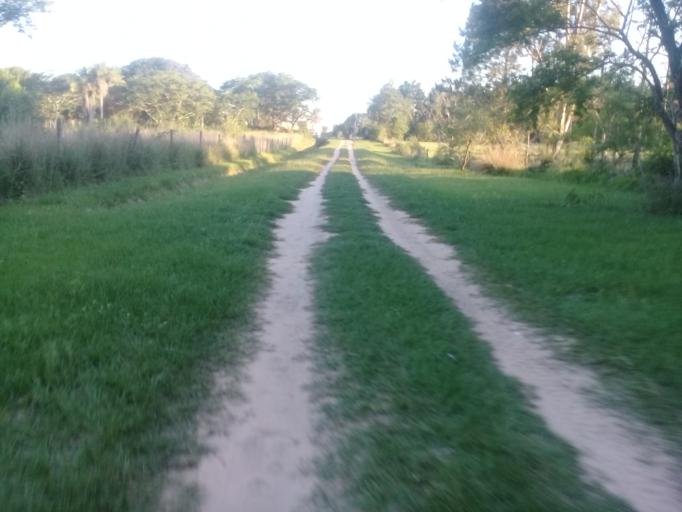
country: AR
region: Corrientes
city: San Luis del Palmar
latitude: -27.4689
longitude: -58.6649
